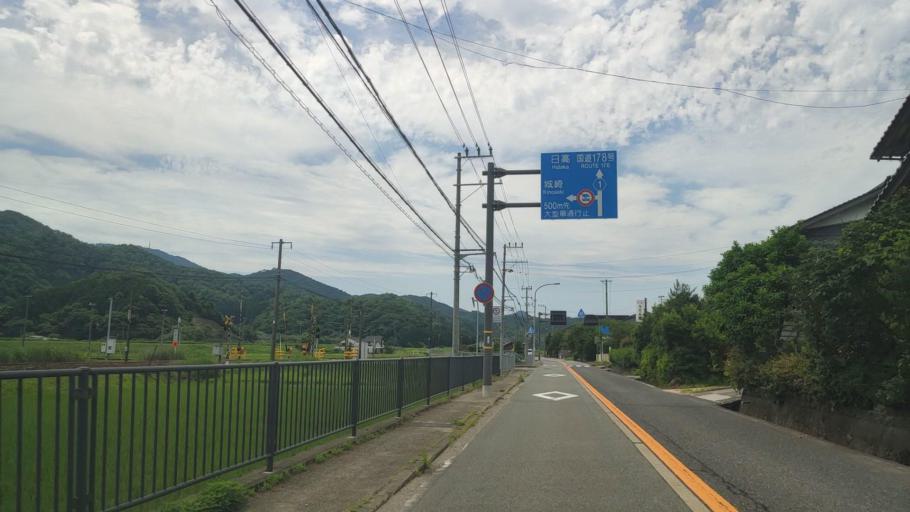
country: JP
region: Hyogo
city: Toyooka
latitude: 35.6439
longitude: 134.7581
